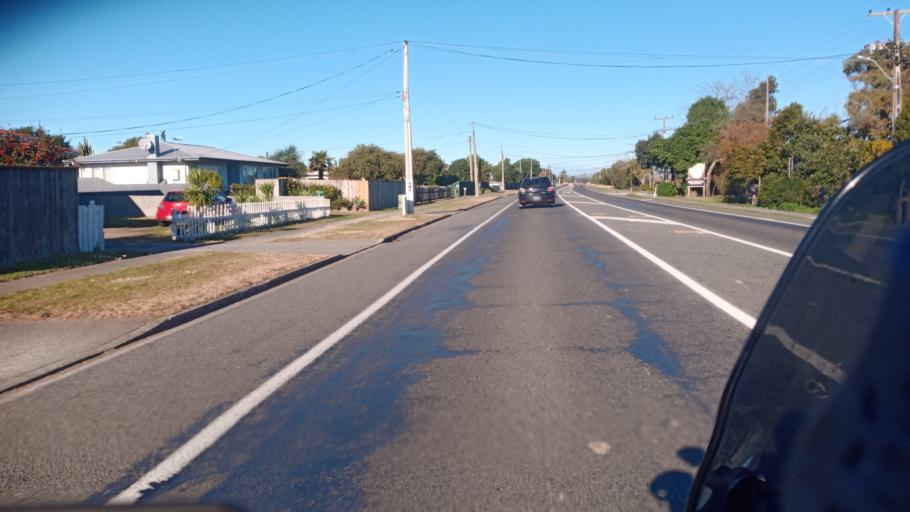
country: NZ
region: Hawke's Bay
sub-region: Napier City
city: Napier
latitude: -39.4311
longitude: 176.8717
